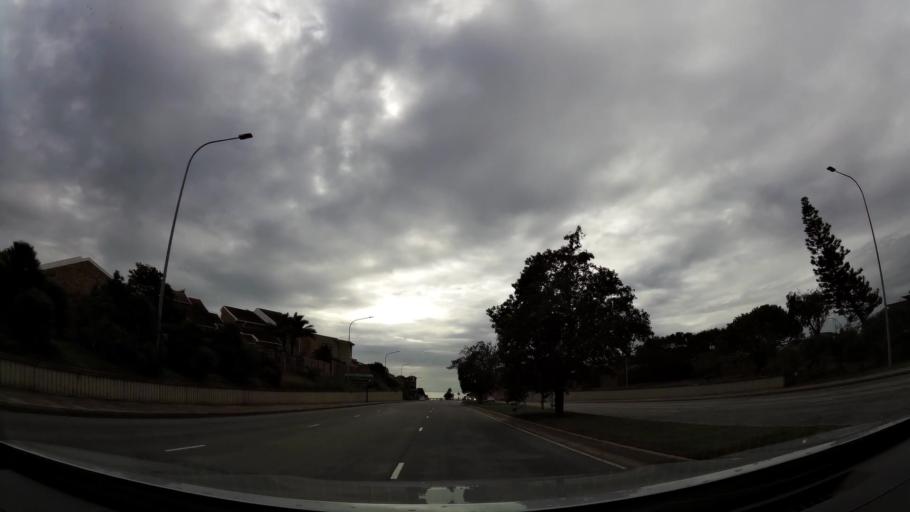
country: ZA
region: Eastern Cape
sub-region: Nelson Mandela Bay Metropolitan Municipality
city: Port Elizabeth
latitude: -33.9726
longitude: 25.6218
